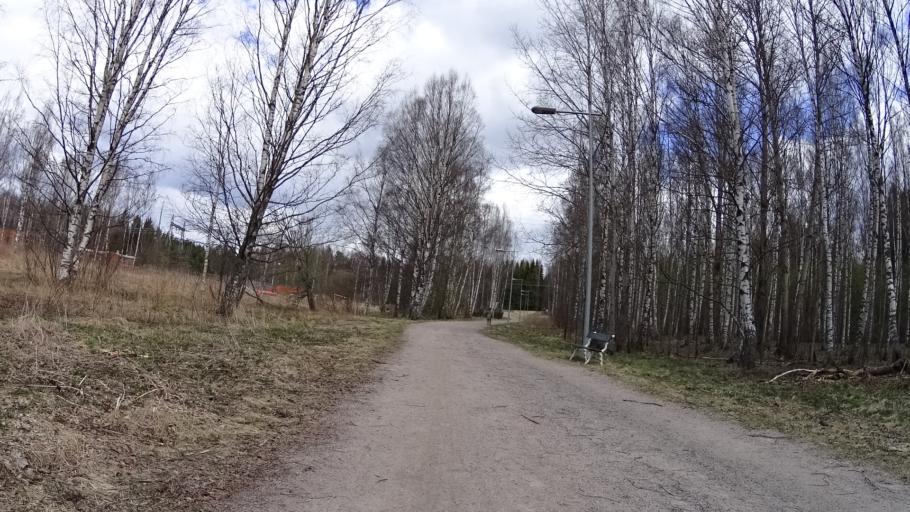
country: FI
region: Uusimaa
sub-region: Helsinki
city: Kilo
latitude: 60.2400
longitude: 24.7973
